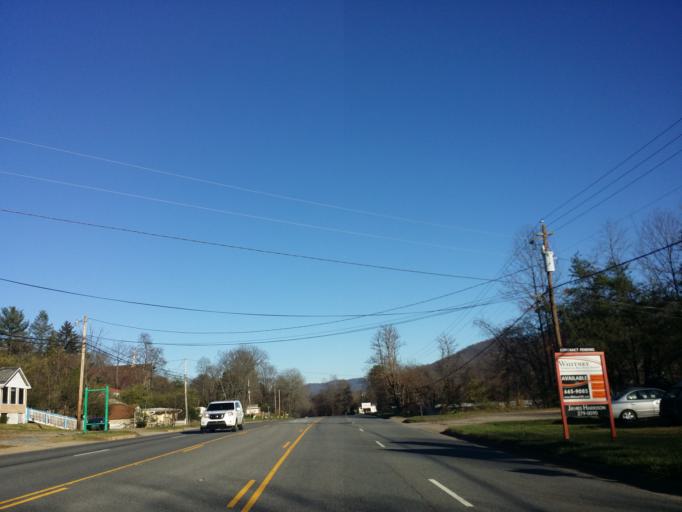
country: US
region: North Carolina
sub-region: Buncombe County
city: Swannanoa
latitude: 35.5967
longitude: -82.4193
